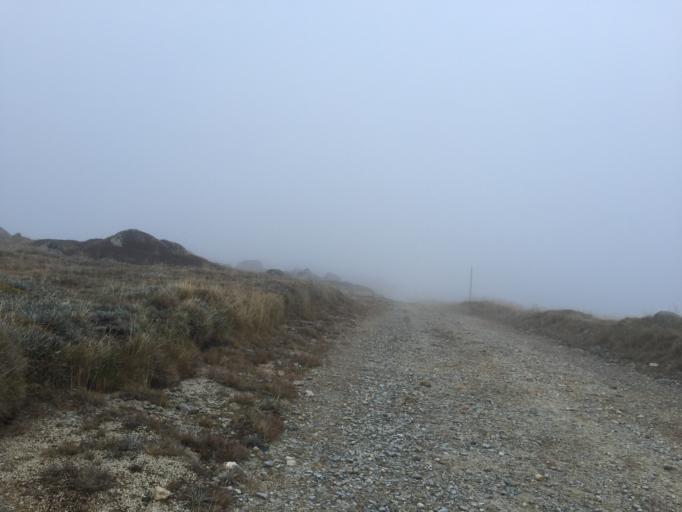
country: AU
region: New South Wales
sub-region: Snowy River
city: Jindabyne
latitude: -36.4518
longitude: 148.2866
